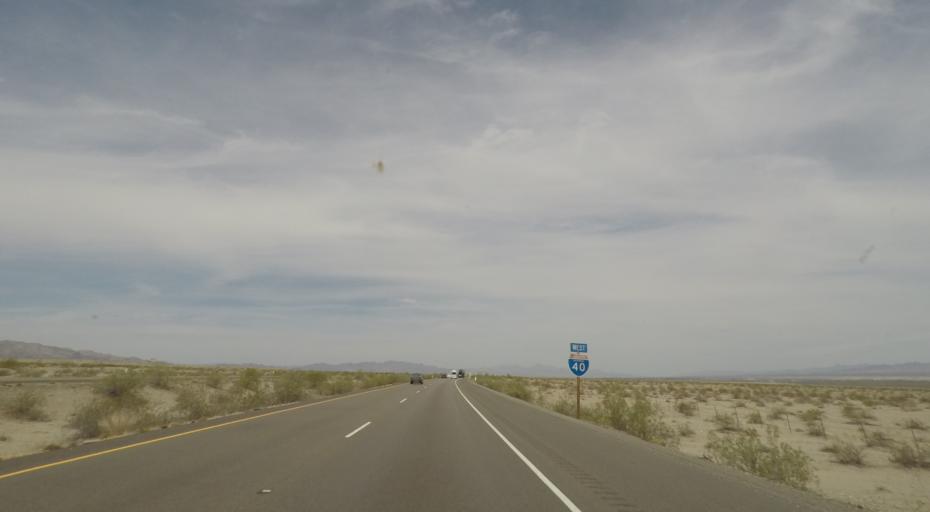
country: US
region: California
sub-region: San Bernardino County
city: Needles
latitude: 34.7689
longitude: -114.5787
